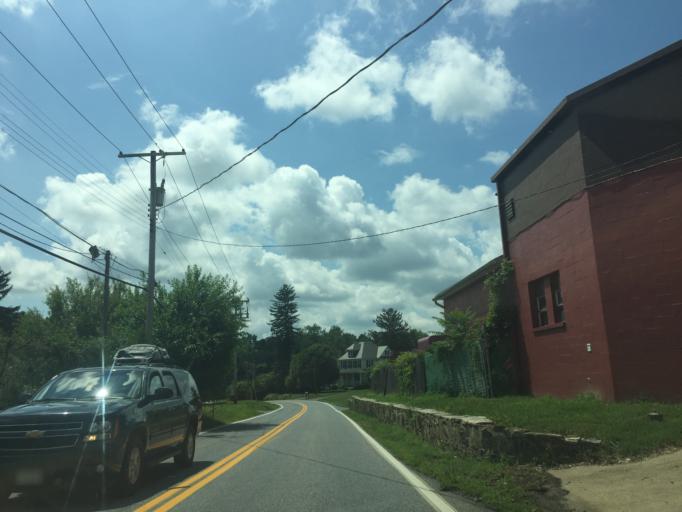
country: US
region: Maryland
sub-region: Baltimore County
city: Kingsville
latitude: 39.4484
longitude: -76.4177
